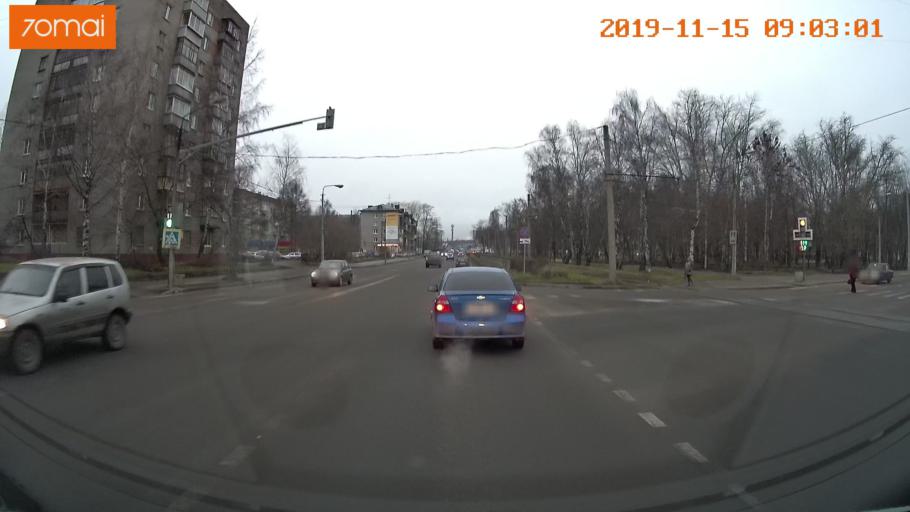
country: RU
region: Vologda
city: Cherepovets
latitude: 59.1372
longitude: 37.9252
